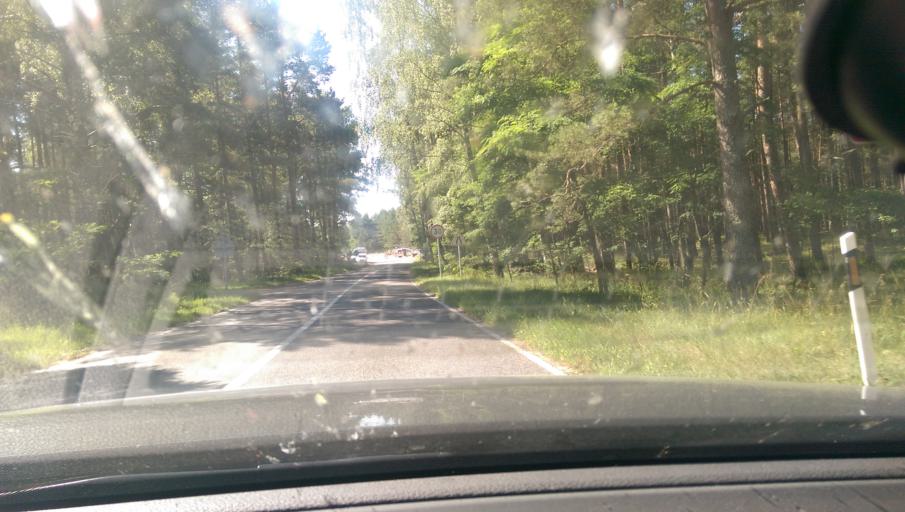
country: LT
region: Klaipedos apskritis
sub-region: Klaipeda
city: Klaipeda
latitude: 55.6804
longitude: 21.1135
